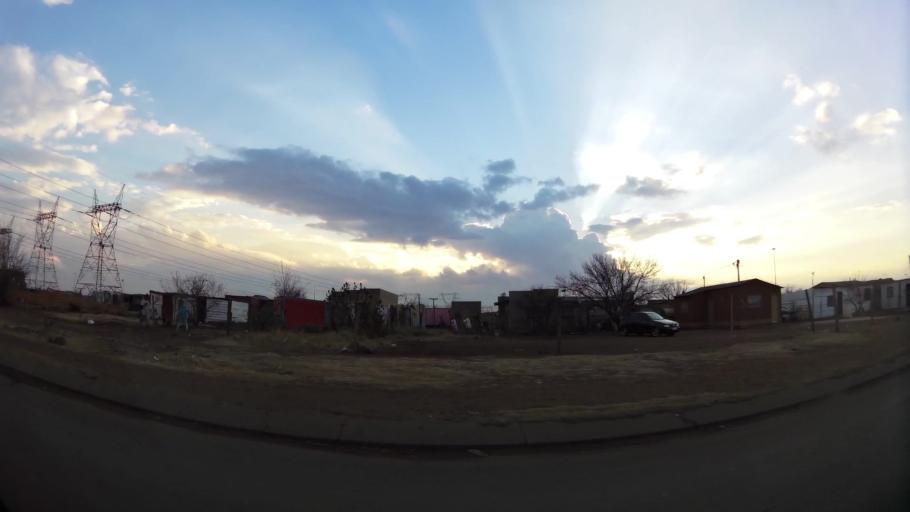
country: ZA
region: Gauteng
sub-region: City of Johannesburg Metropolitan Municipality
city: Orange Farm
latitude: -26.5554
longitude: 27.8394
